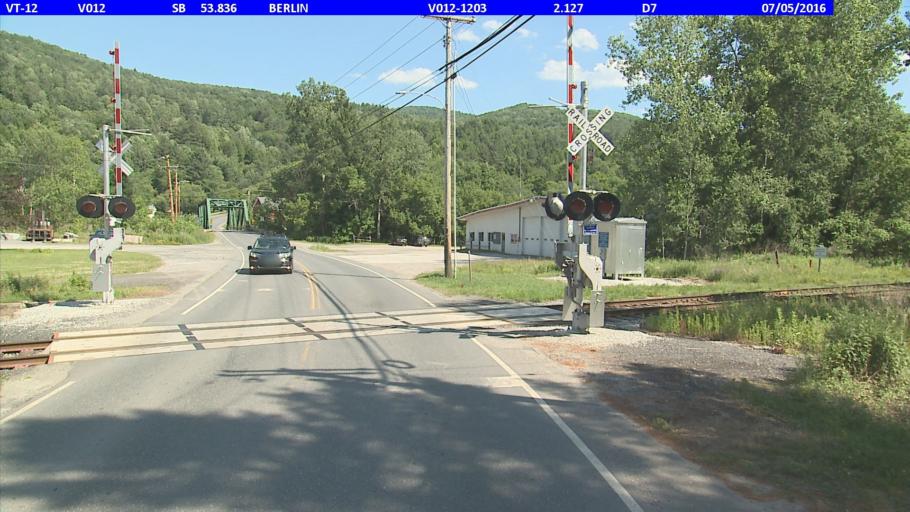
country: US
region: Vermont
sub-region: Washington County
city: Northfield
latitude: 44.2004
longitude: -72.6350
